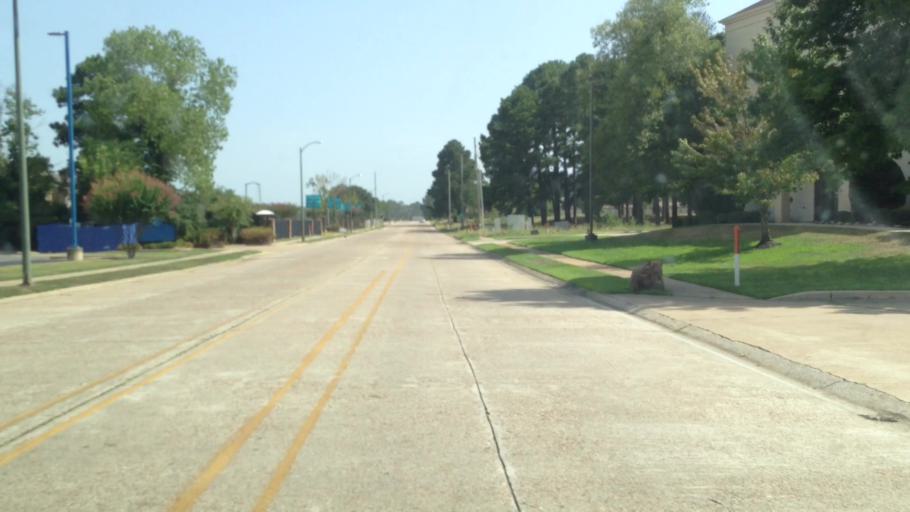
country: US
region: Louisiana
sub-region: Caddo Parish
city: Greenwood
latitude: 32.4512
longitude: -93.8579
